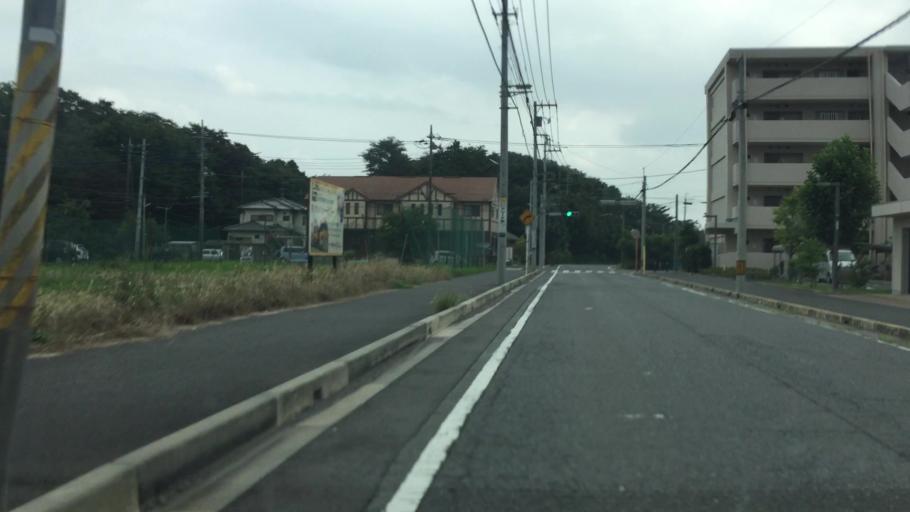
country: JP
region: Chiba
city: Kashiwa
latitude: 35.8086
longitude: 139.9505
